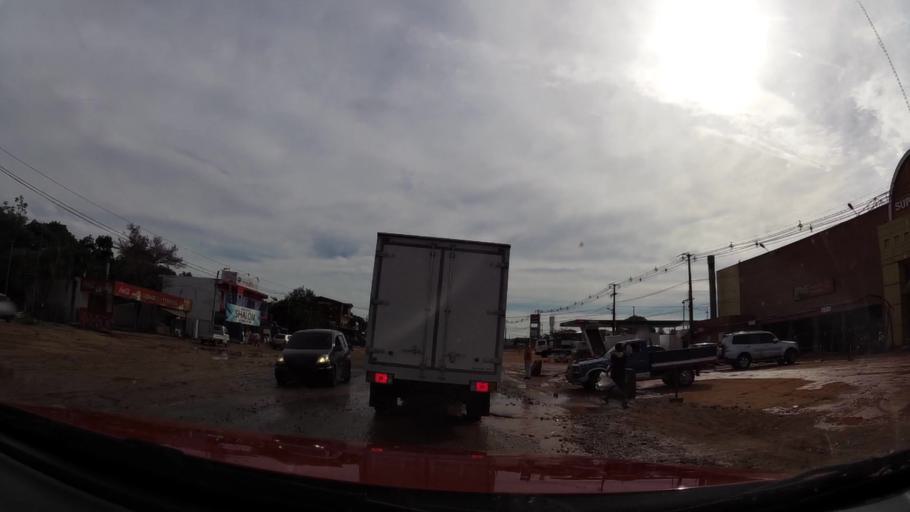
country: PY
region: Central
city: Limpio
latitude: -25.1745
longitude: -57.4836
